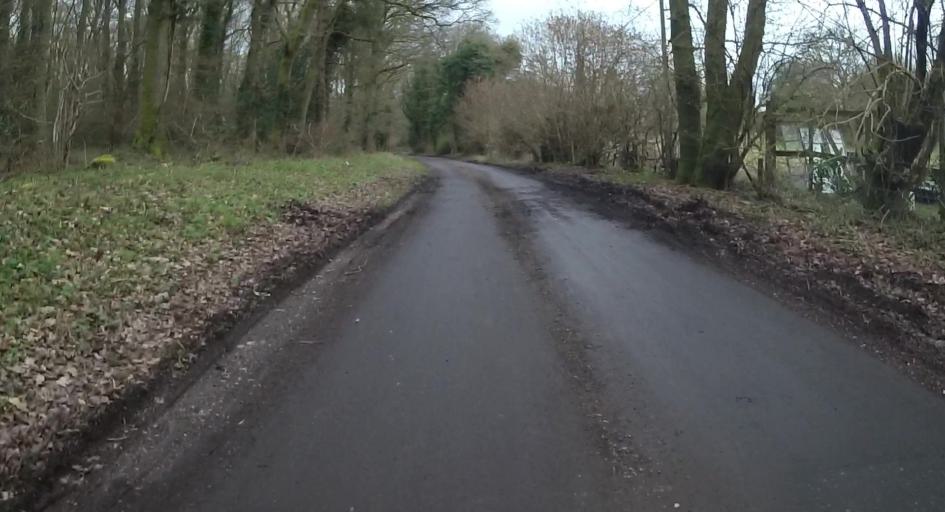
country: GB
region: England
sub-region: Hampshire
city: Kingsclere
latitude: 51.2773
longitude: -1.2019
